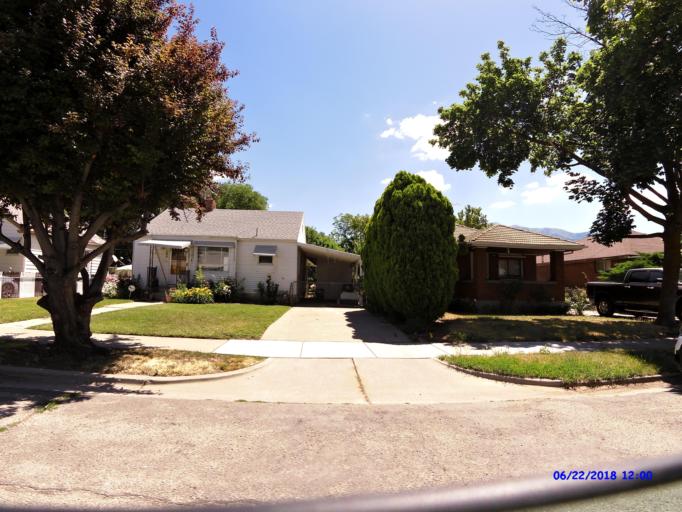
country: US
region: Utah
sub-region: Weber County
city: Ogden
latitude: 41.2384
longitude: -111.9743
